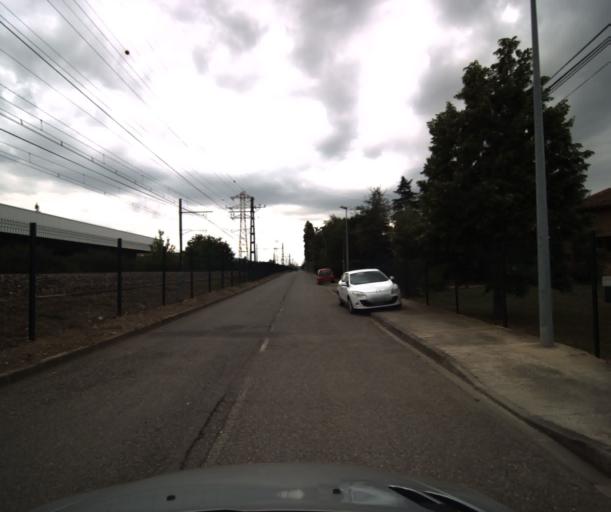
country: FR
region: Midi-Pyrenees
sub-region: Departement de la Haute-Garonne
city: Portet-sur-Garonne
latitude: 43.5408
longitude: 1.3997
